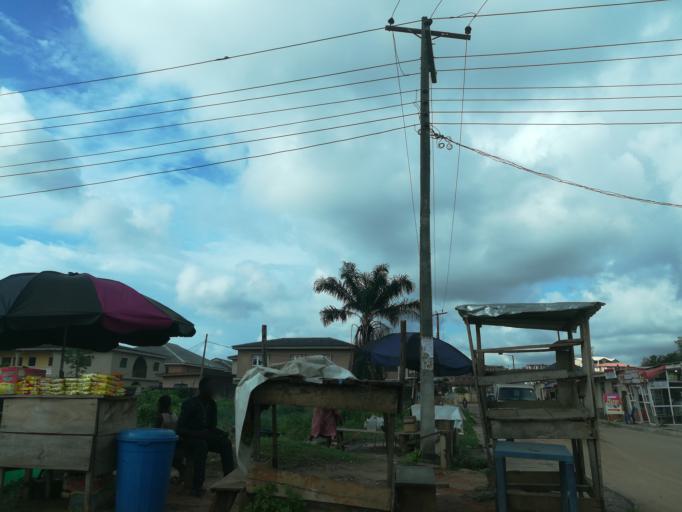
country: NG
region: Lagos
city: Ebute Ikorodu
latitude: 6.5957
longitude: 3.5037
